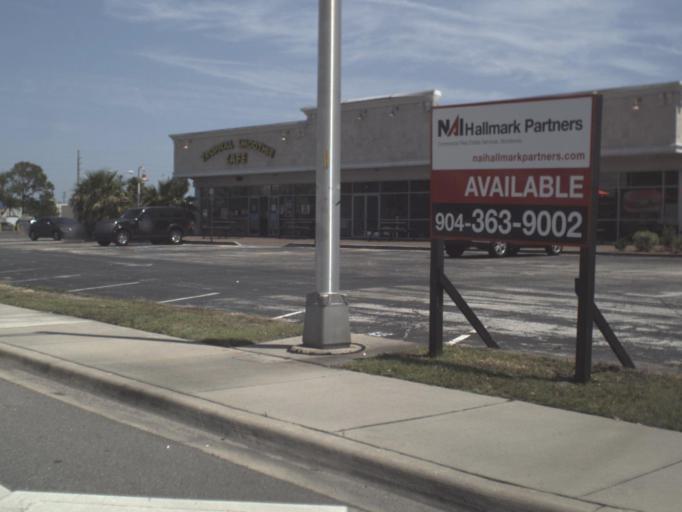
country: US
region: Florida
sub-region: Duval County
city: Jacksonville Beach
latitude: 30.2881
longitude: -81.4030
